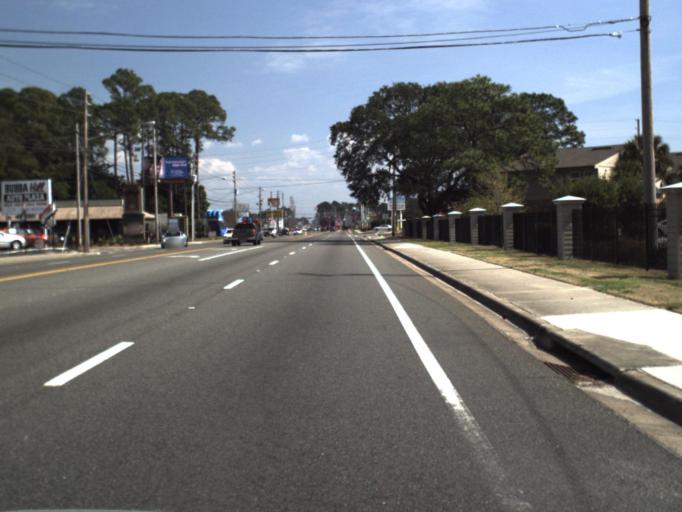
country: US
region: Florida
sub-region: Bay County
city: Pretty Bayou
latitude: 30.1897
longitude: -85.7050
